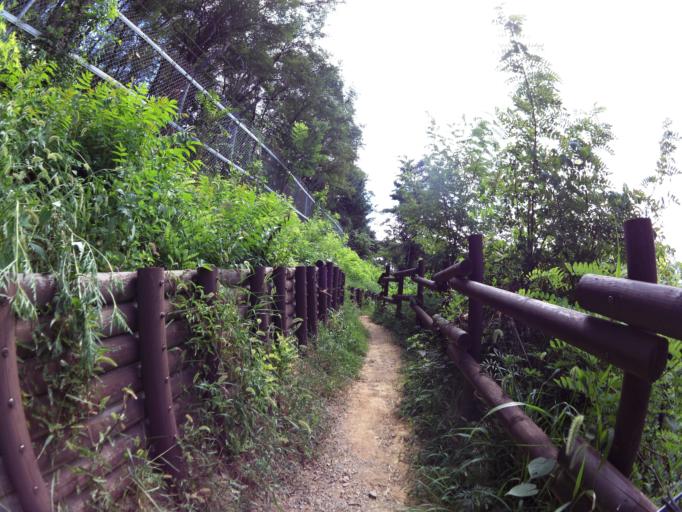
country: KR
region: Daegu
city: Daegu
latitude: 35.8607
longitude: 128.6556
